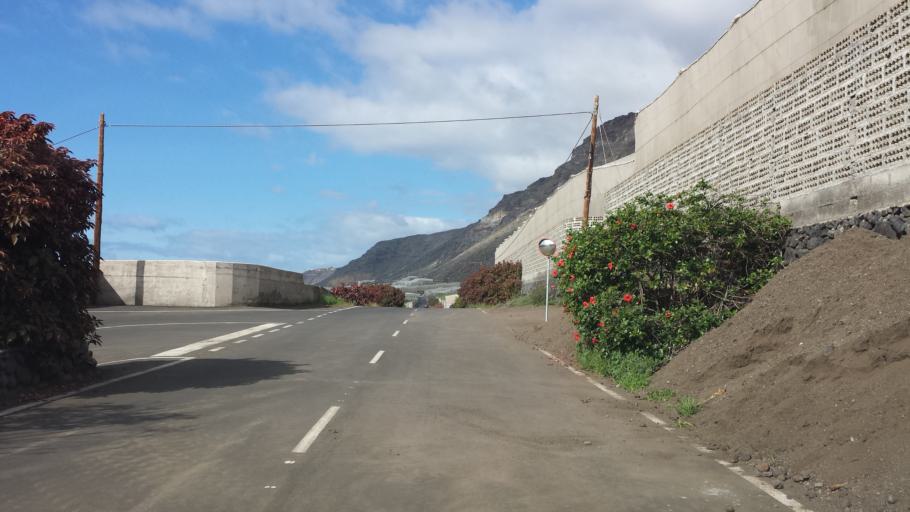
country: ES
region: Canary Islands
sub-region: Provincia de Santa Cruz de Tenerife
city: Fuencaliente de la Palma
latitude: 28.5526
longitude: -17.8861
